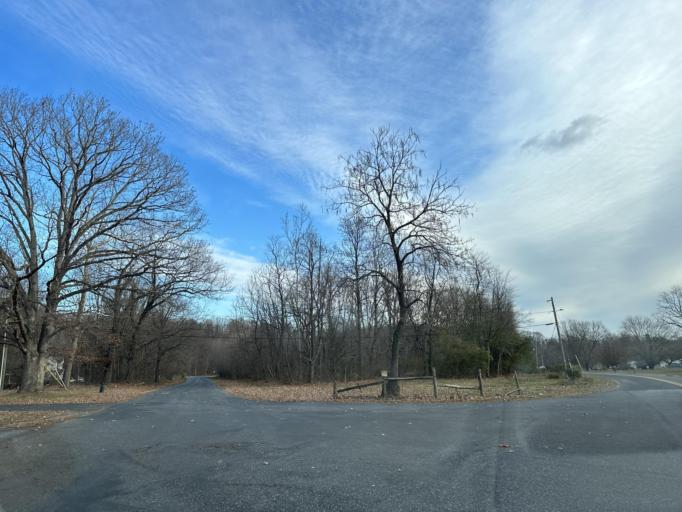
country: US
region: Virginia
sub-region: City of Staunton
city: Staunton
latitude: 38.2136
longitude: -79.2186
